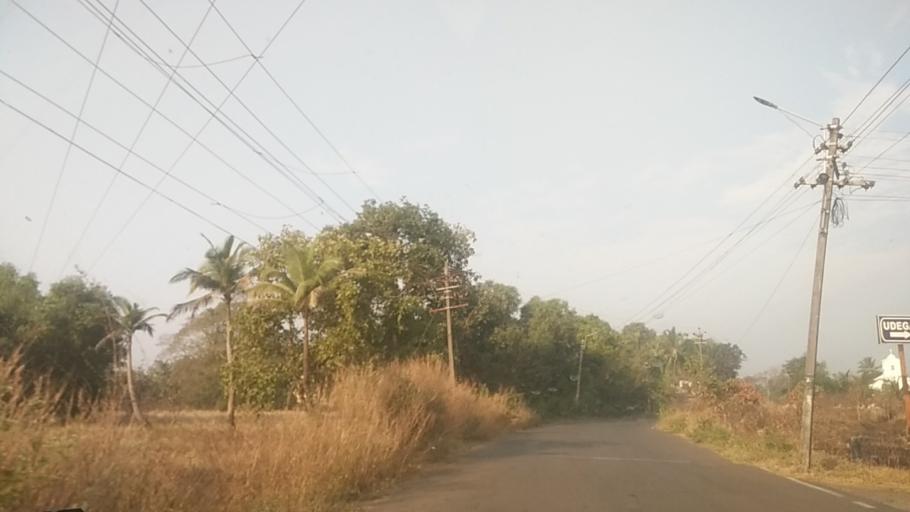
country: IN
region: Goa
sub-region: South Goa
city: Chinchinim
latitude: 15.2339
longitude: 73.9877
